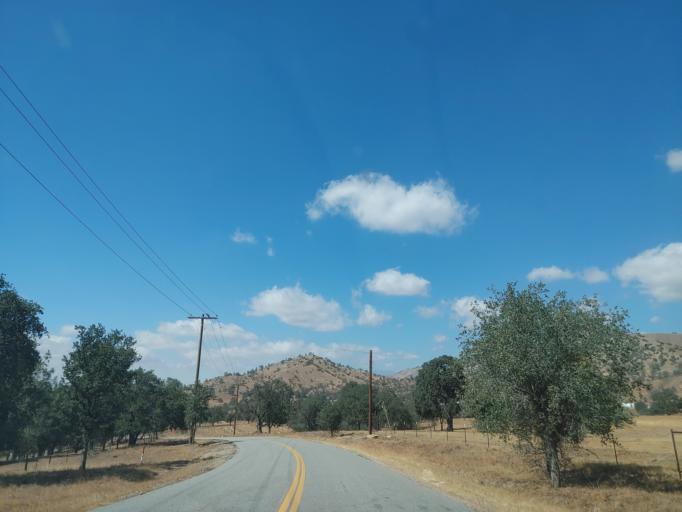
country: US
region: California
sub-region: Kern County
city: Golden Hills
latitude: 35.2045
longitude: -118.5430
